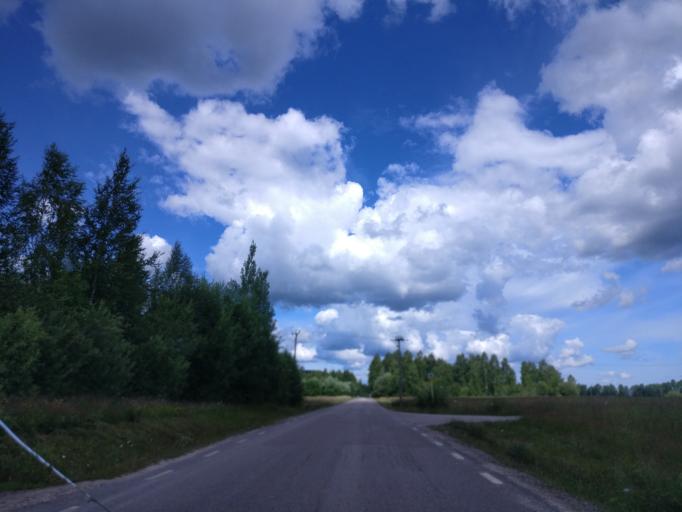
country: SE
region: Vaermland
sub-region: Hagfors Kommun
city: Ekshaerad
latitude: 60.0392
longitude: 13.4974
